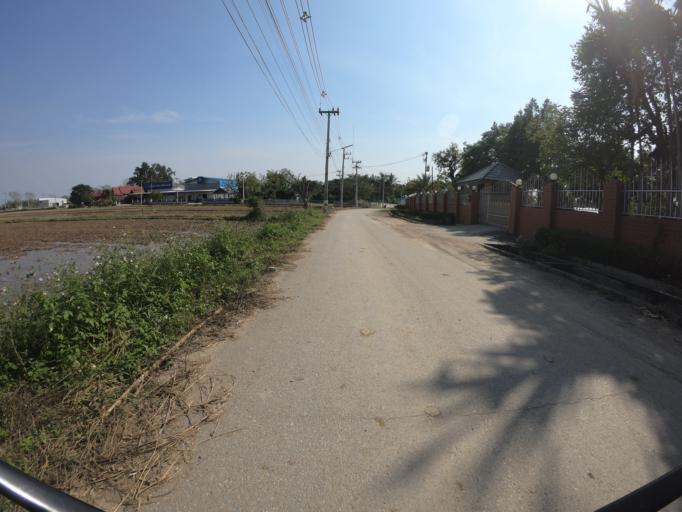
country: TH
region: Chiang Mai
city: San Sai
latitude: 18.8561
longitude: 98.9978
